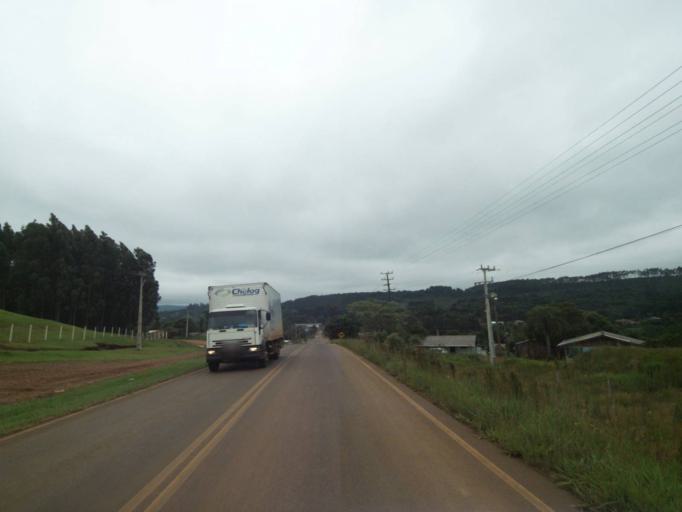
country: BR
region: Parana
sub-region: Pitanga
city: Pitanga
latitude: -24.9309
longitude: -51.8757
